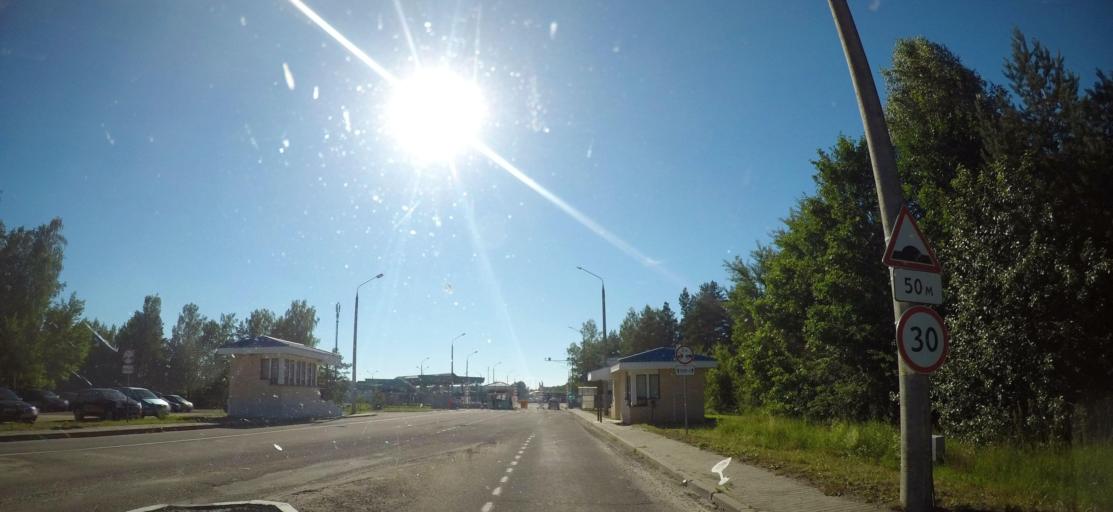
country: BY
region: Grodnenskaya
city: Vyalikaya Byerastavitsa
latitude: 53.1225
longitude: 23.9017
